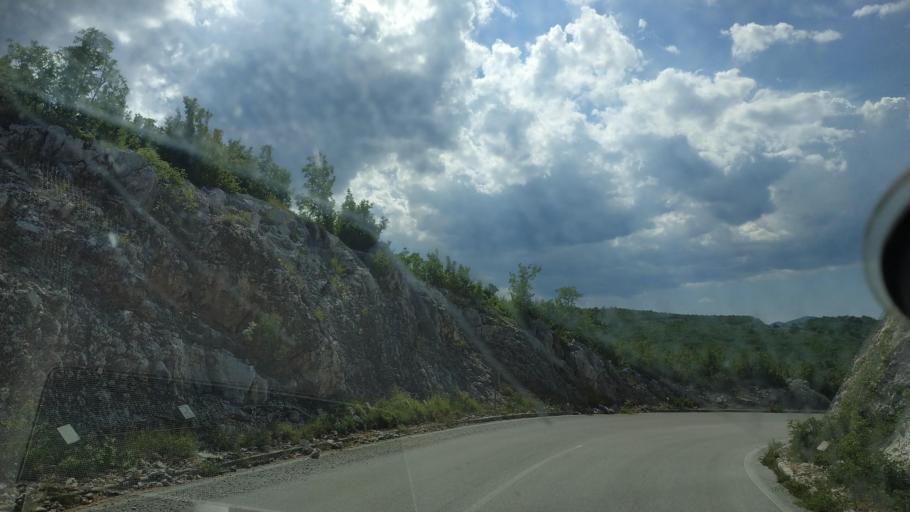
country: HR
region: Splitsko-Dalmatinska
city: Dugopolje
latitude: 43.5830
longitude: 16.6507
